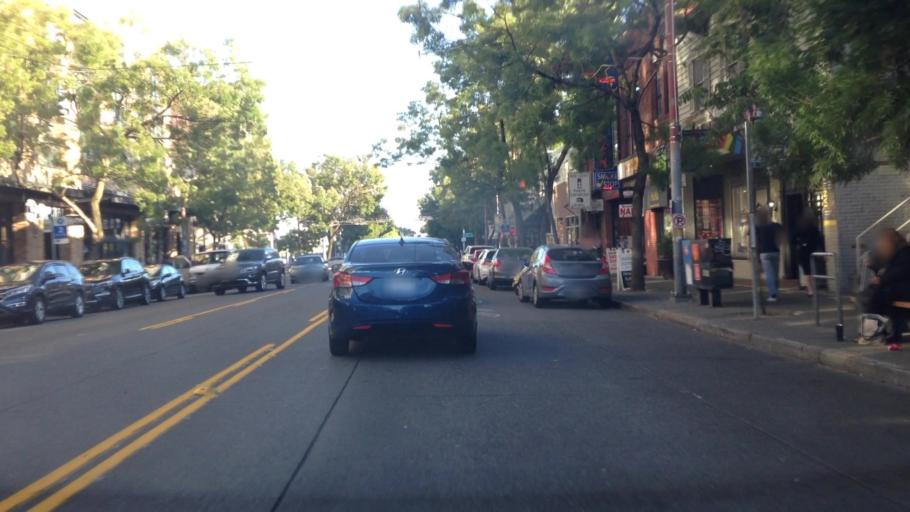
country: US
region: Washington
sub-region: King County
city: Seattle
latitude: 47.6209
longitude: -122.3209
